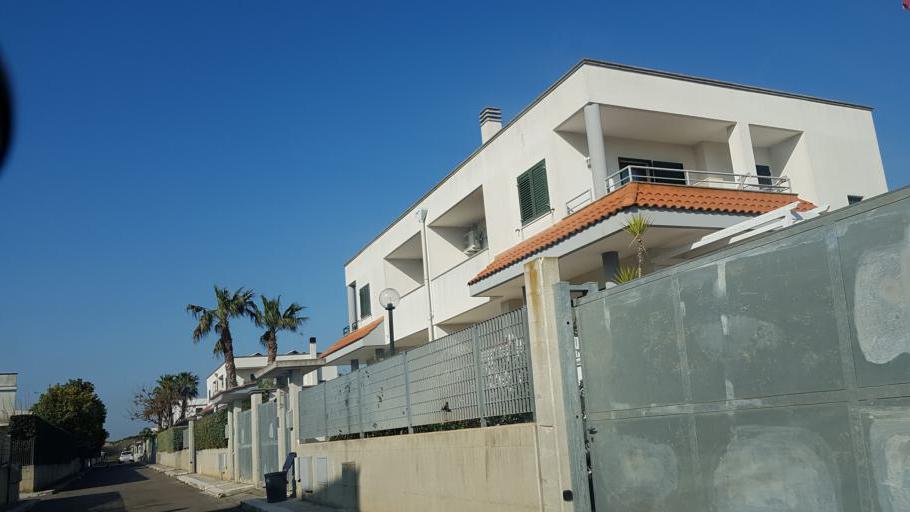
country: IT
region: Apulia
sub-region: Provincia di Brindisi
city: Brindisi
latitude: 40.6467
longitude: 17.9263
